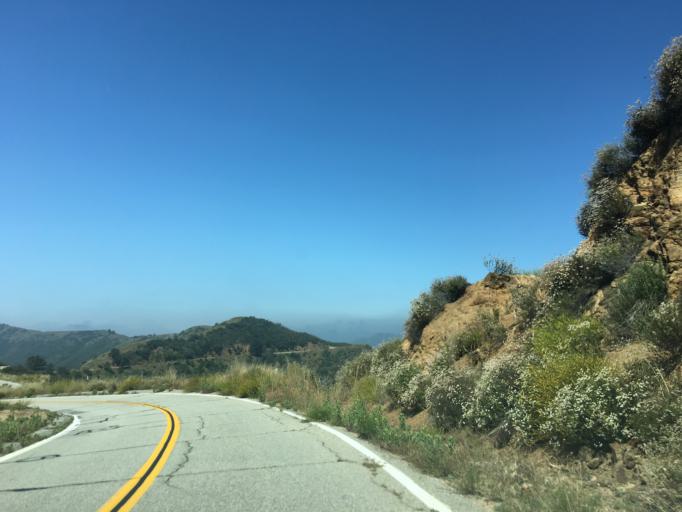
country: US
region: California
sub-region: Los Angeles County
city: Glendora
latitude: 34.2019
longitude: -117.8243
